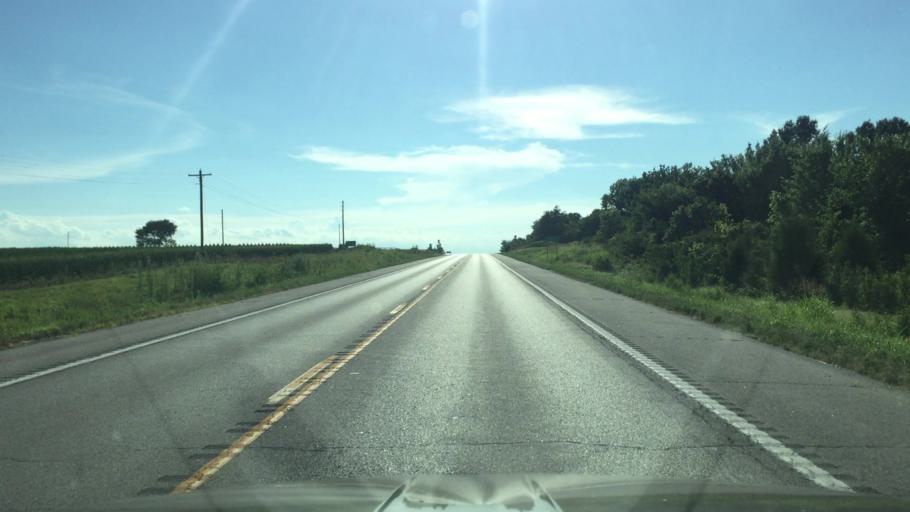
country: US
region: Missouri
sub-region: Pettis County
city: Sedalia
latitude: 38.6937
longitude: -93.0944
